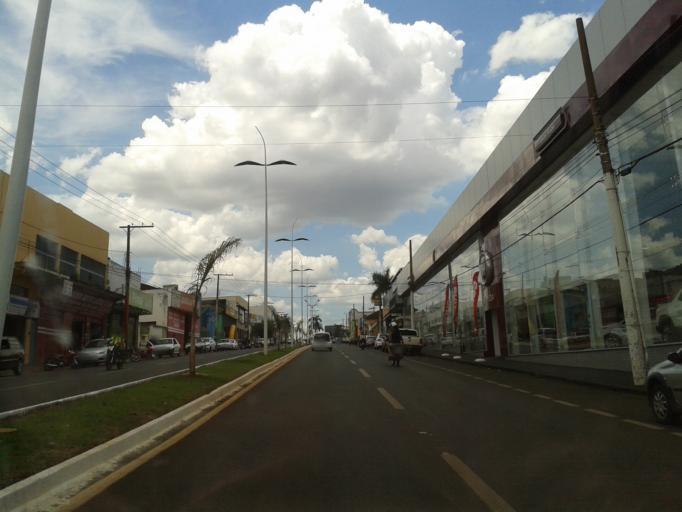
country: BR
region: Goias
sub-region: Itumbiara
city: Itumbiara
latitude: -18.4081
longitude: -49.2119
